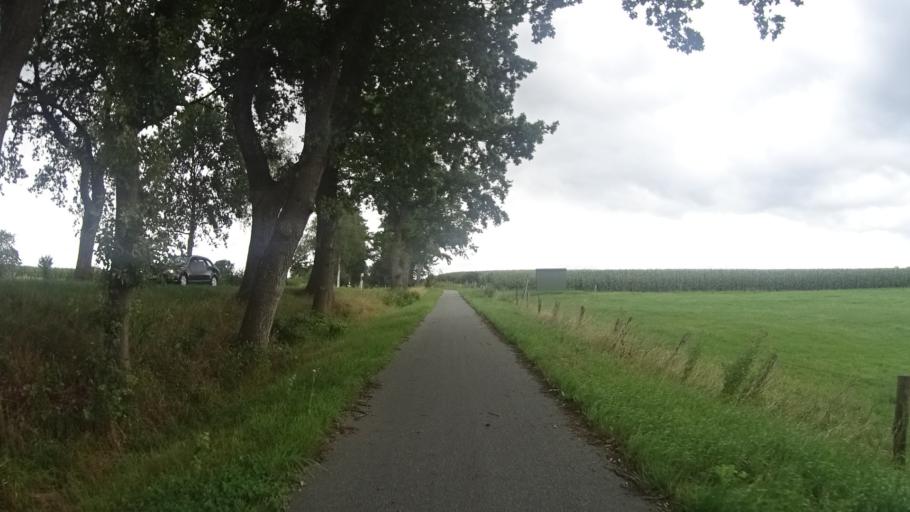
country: DE
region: Lower Saxony
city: Kuhrstedt
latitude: 53.5921
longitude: 8.8097
